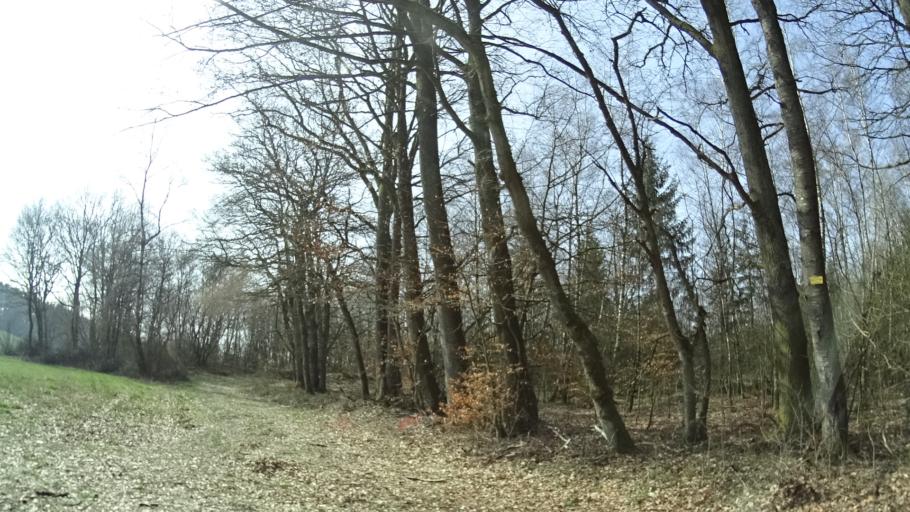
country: DE
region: Rheinland-Pfalz
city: Ruschberg
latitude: 49.6065
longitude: 7.2795
